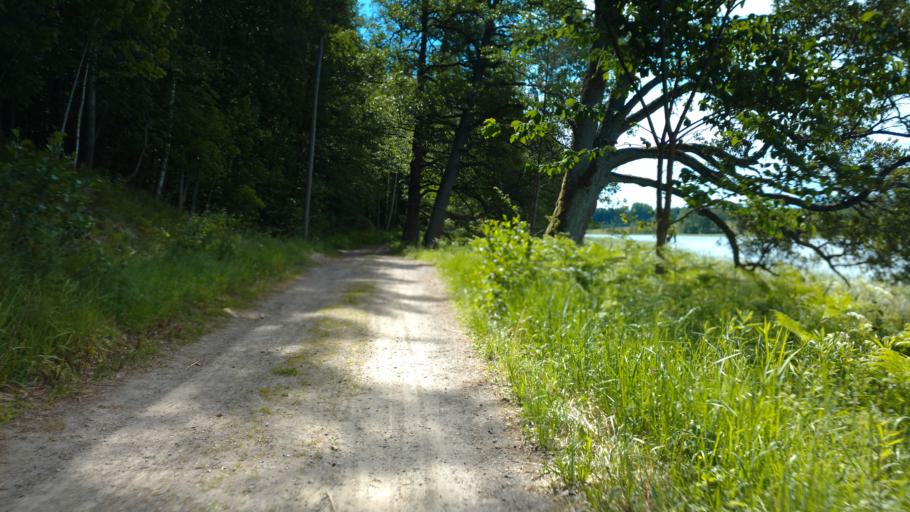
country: FI
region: Uusimaa
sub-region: Raaseporin
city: Pohja
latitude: 60.1163
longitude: 23.5422
